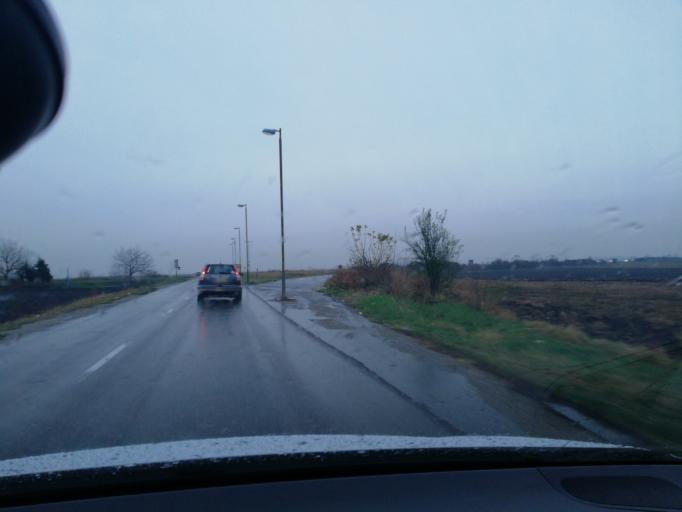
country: RS
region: Autonomna Pokrajina Vojvodina
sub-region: Sremski Okrug
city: Ruma
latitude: 44.9850
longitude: 19.8186
